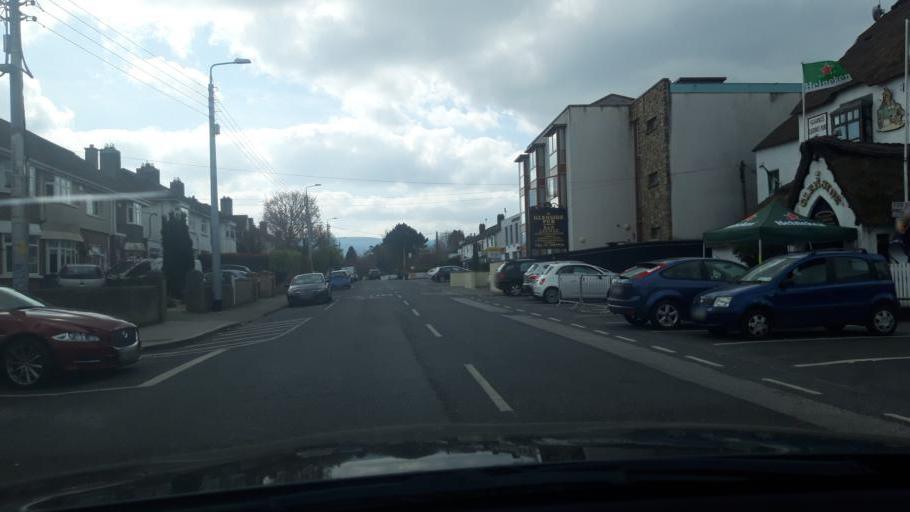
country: IE
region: Leinster
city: Dundrum
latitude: 53.2999
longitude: -6.2676
